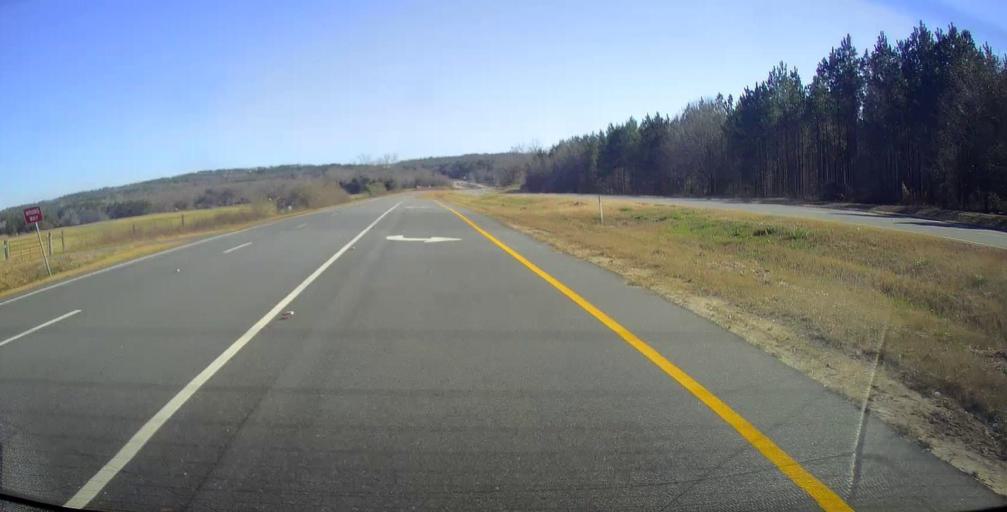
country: US
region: Georgia
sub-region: Taylor County
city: Butler
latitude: 32.6249
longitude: -84.2501
